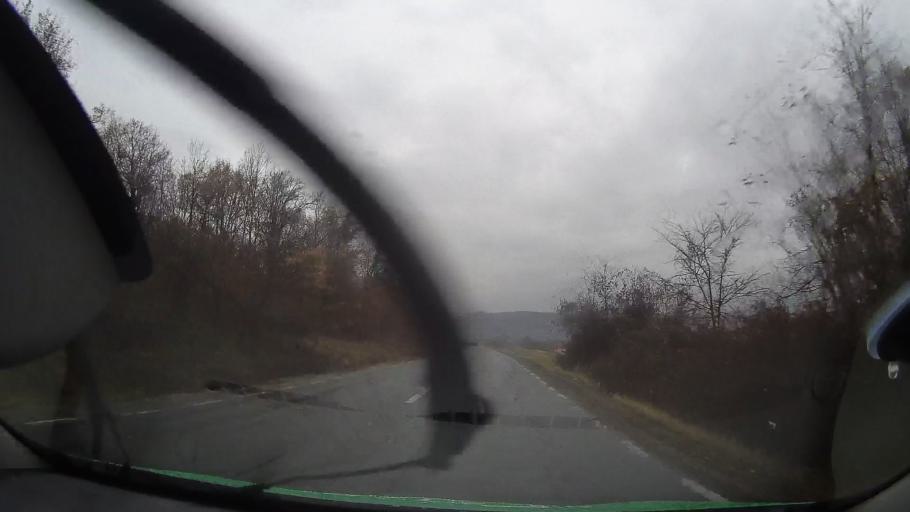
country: RO
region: Bihor
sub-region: Comuna Rabagani
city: Rabagani
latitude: 46.7362
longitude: 22.2305
